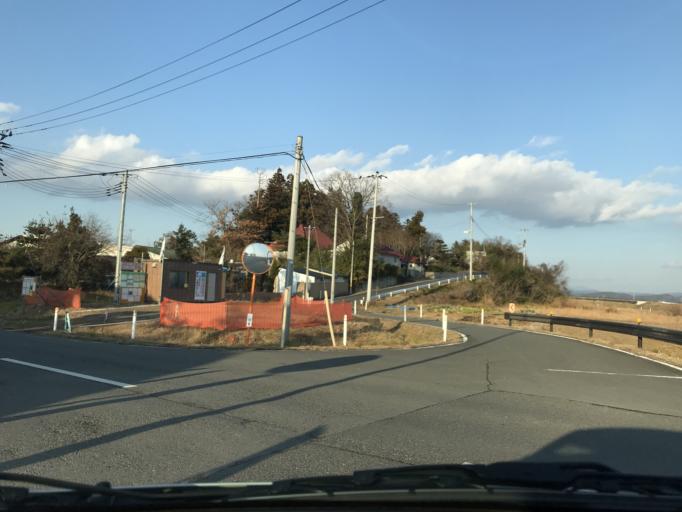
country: JP
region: Miyagi
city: Wakuya
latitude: 38.7124
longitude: 141.1469
